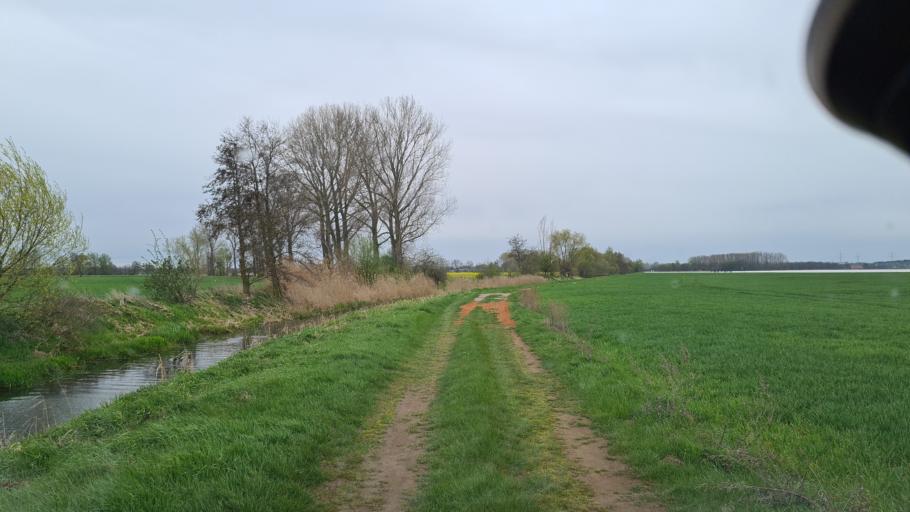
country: DE
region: Brandenburg
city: Doberlug-Kirchhain
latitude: 51.6617
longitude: 13.5658
